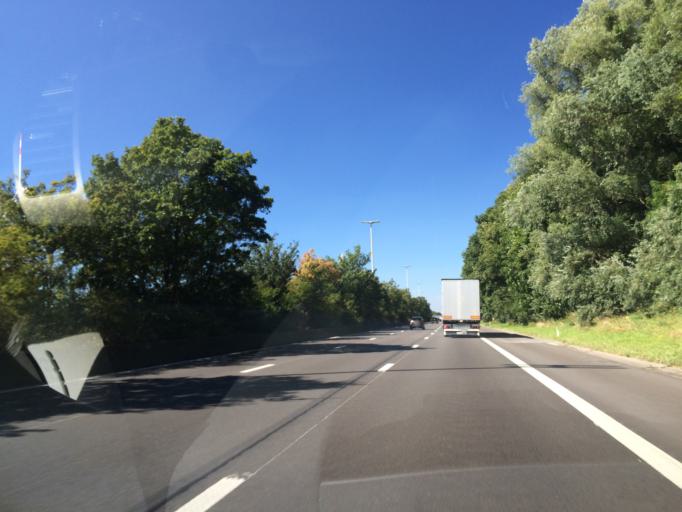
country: BE
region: Wallonia
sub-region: Province du Brabant Wallon
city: Perwez
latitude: 50.5945
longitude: 4.7977
